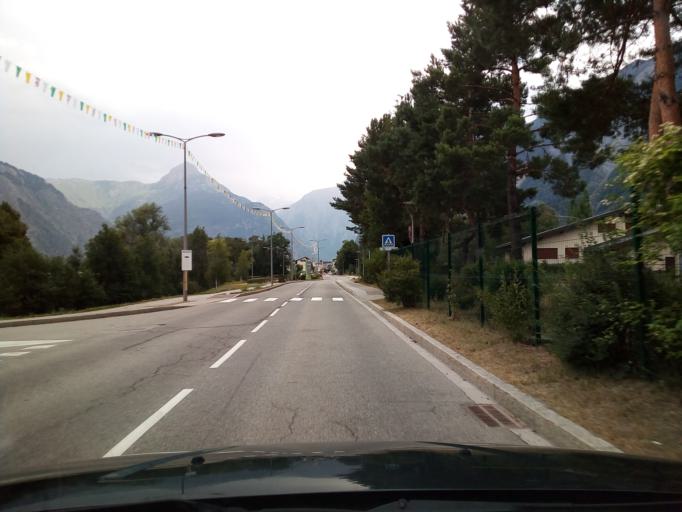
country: FR
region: Rhone-Alpes
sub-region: Departement de l'Isere
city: Huez
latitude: 45.0624
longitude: 6.0254
